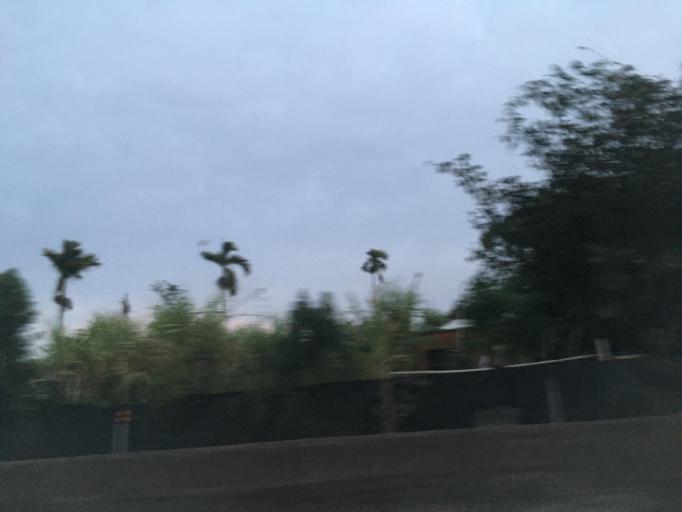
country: TW
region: Taiwan
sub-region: Chiayi
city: Jiayi Shi
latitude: 23.5820
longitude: 120.4611
